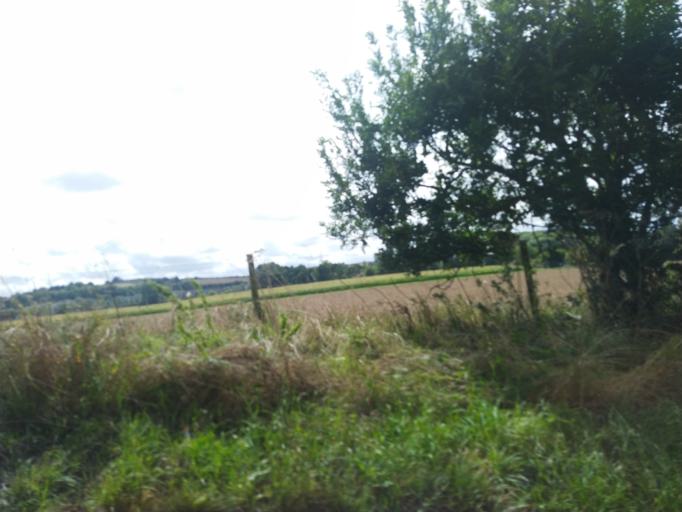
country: GB
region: England
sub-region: Dorset
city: Blandford Forum
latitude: 50.8269
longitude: -2.1158
